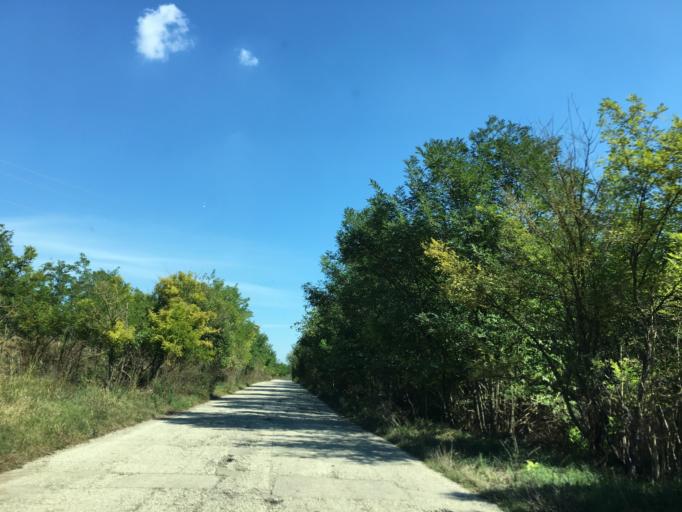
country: BG
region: Pleven
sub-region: Obshtina Knezha
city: Knezha
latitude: 43.5439
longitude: 24.1540
